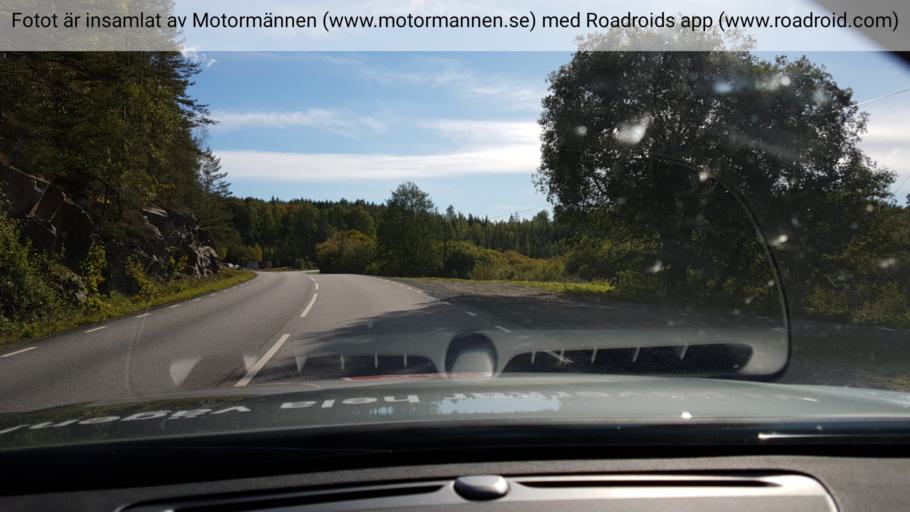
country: SE
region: OEstergoetland
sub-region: Valdemarsviks Kommun
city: Valdemarsvik
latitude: 58.1826
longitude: 16.5796
